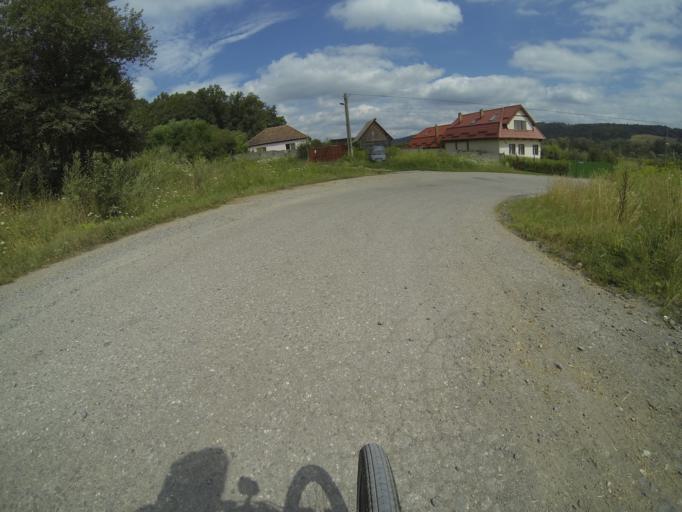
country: RO
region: Brasov
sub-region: Comuna Hoghiz
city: Hoghiz
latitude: 45.9815
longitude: 25.3530
